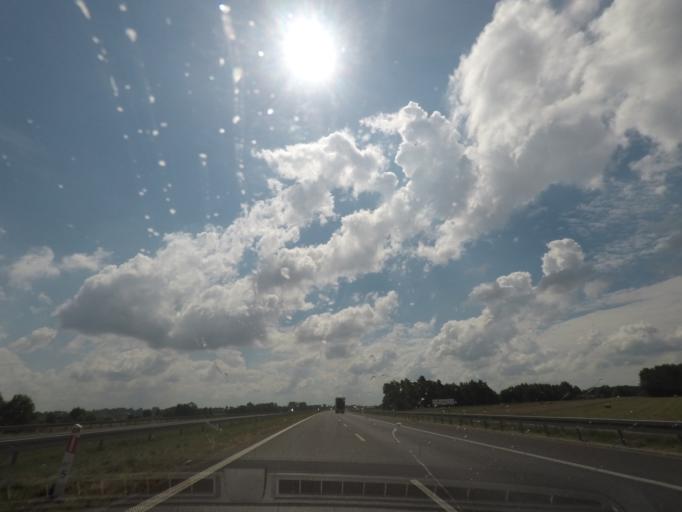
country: PL
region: Lodz Voivodeship
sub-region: Powiat zgierski
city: Strykow
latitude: 51.9455
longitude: 19.6080
